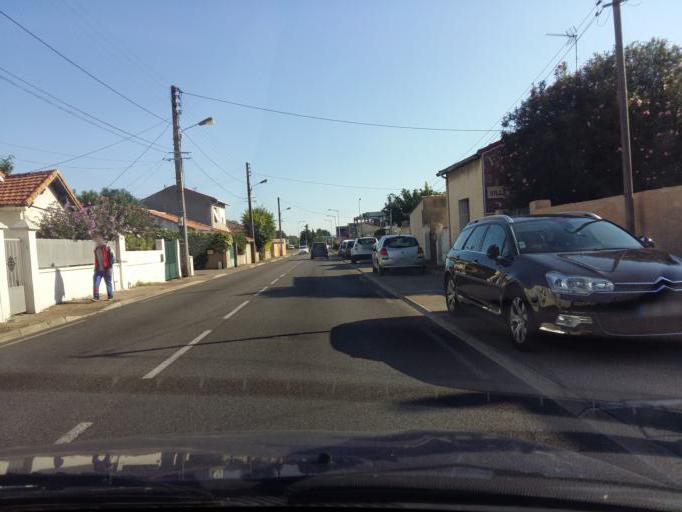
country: FR
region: Languedoc-Roussillon
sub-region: Departement du Gard
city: Nimes
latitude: 43.8162
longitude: 4.3531
